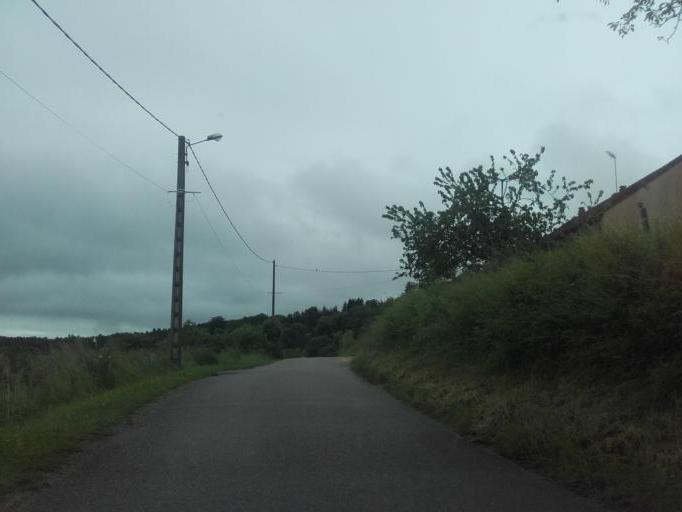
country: FR
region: Bourgogne
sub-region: Departement de la Cote-d'Or
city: Nolay
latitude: 46.9744
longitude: 4.6821
